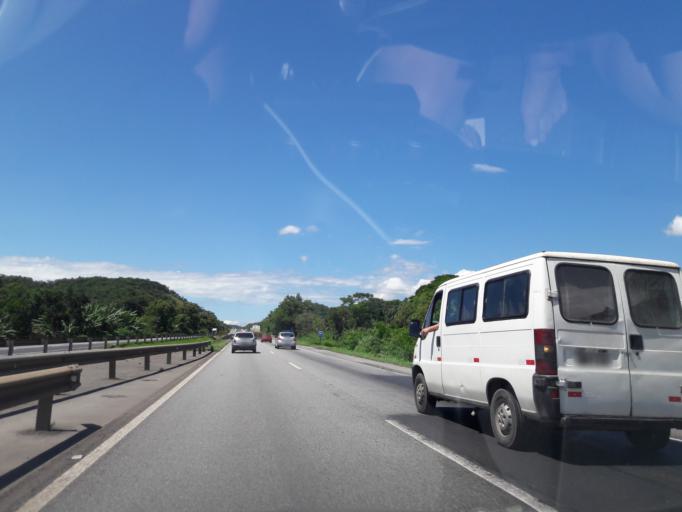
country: BR
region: Parana
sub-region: Antonina
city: Antonina
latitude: -25.5357
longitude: -48.7632
